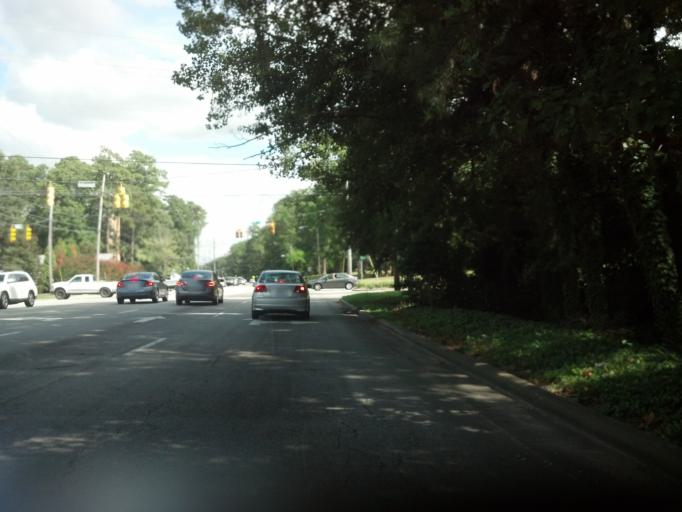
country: US
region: North Carolina
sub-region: Pitt County
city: Greenville
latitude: 35.5901
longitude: -77.3612
